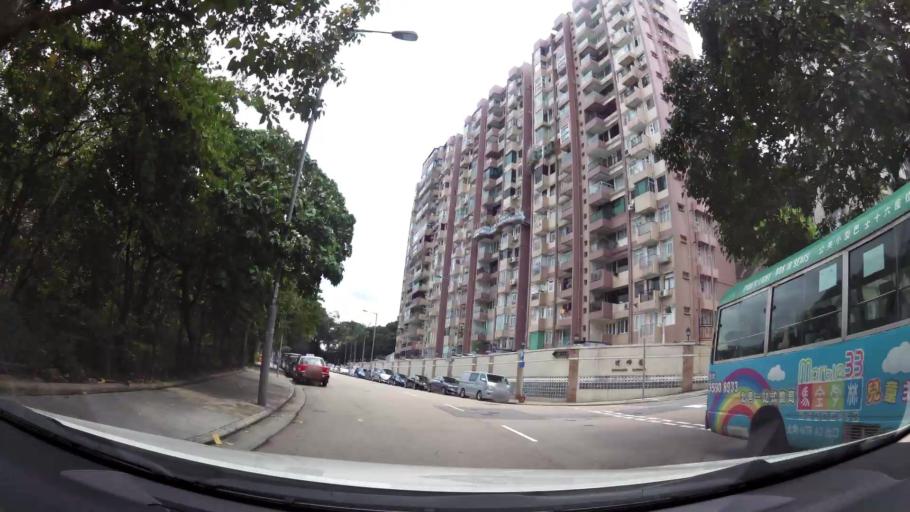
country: HK
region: Wanchai
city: Wan Chai
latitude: 22.2881
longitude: 114.2049
